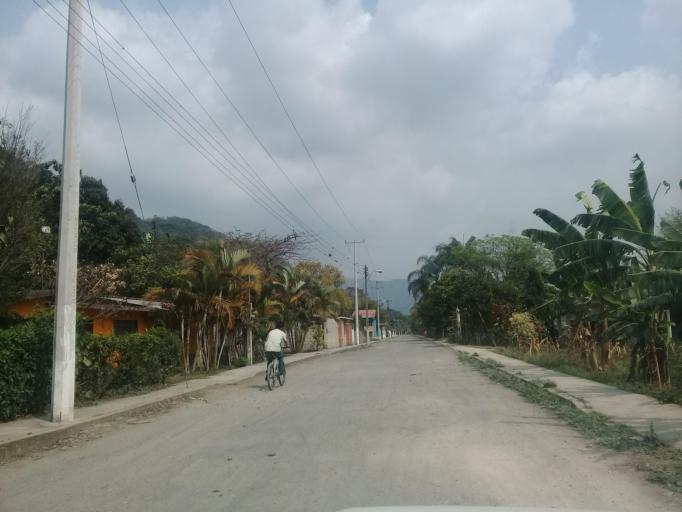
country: MX
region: Veracruz
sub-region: Ixtaczoquitlan
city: Capoluca
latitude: 18.8168
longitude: -96.9927
